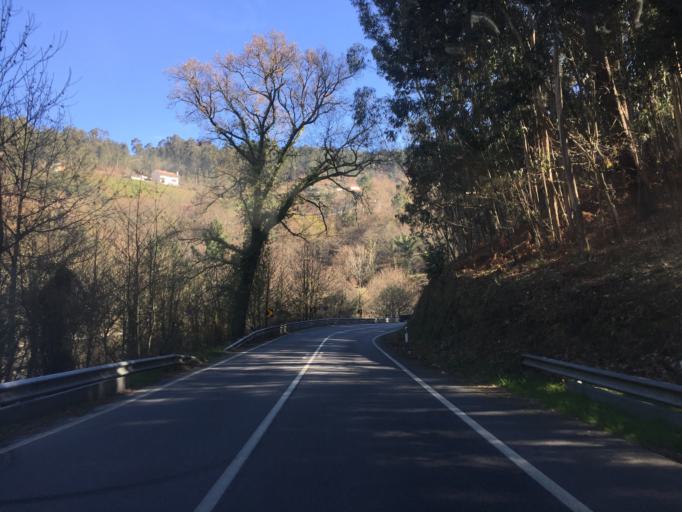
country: PT
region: Aveiro
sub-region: Vale de Cambra
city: Macieira de Cambra
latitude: 40.8956
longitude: -8.3273
